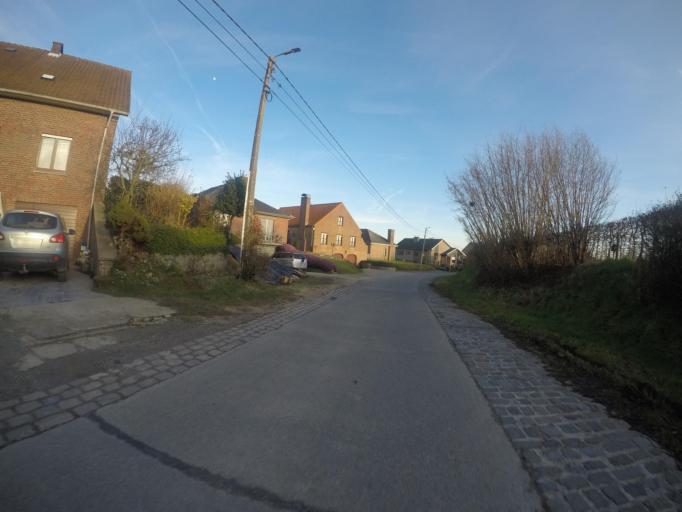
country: BE
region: Flanders
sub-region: Provincie Vlaams-Brabant
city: Pepingen
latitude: 50.7418
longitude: 4.1780
